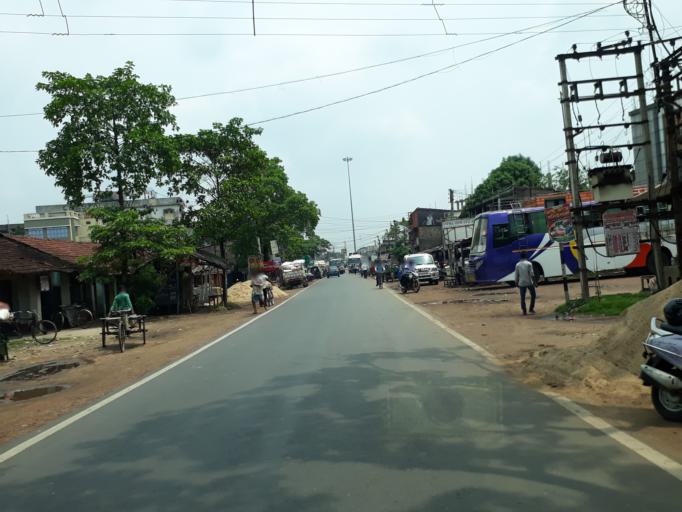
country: IN
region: West Bengal
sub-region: Purba Medinipur
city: Mahishadal
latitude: 22.1870
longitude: 87.9182
